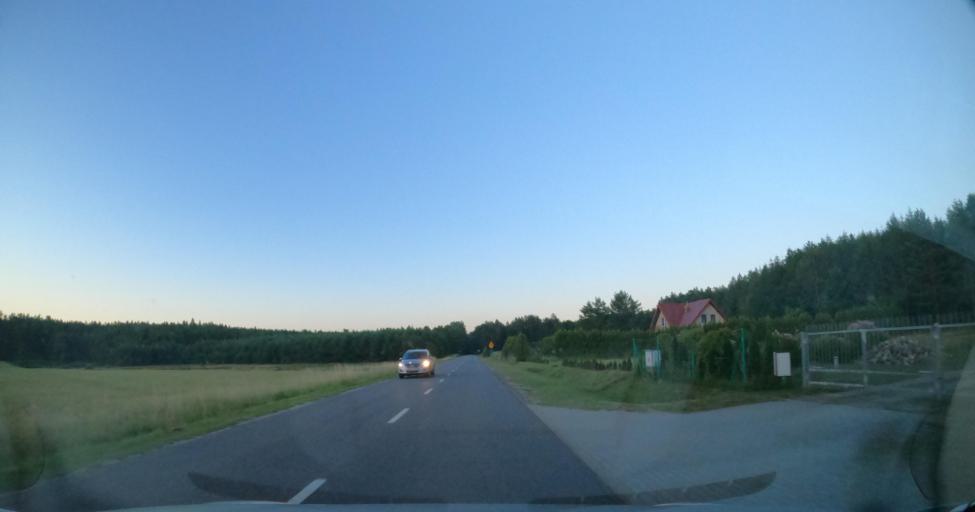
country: PL
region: Pomeranian Voivodeship
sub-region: Powiat wejherowski
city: Linia
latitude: 54.4576
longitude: 17.9497
